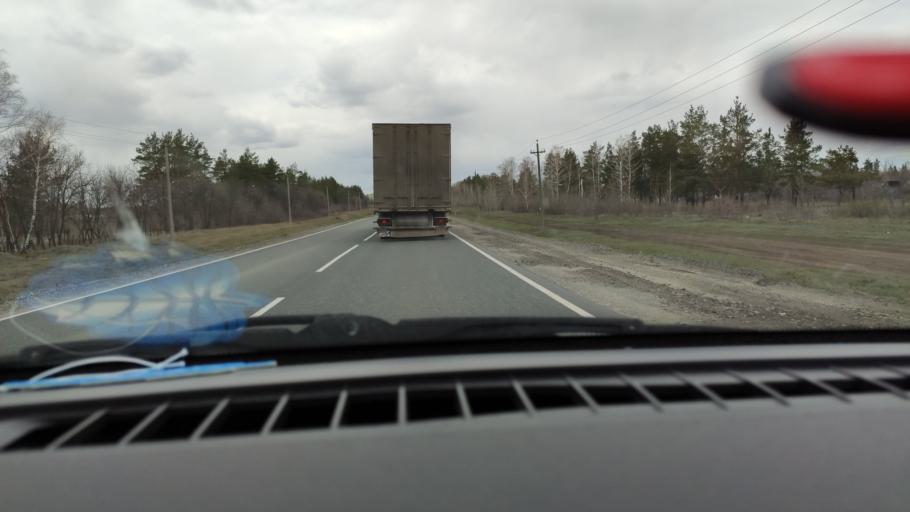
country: RU
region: Saratov
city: Sennoy
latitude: 52.1519
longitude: 46.9676
